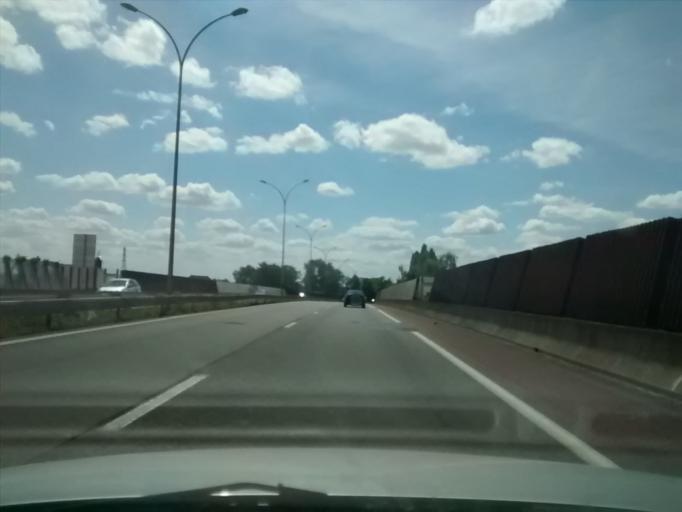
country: FR
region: Pays de la Loire
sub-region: Departement de la Sarthe
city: Le Mans
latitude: 48.0046
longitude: 0.1726
